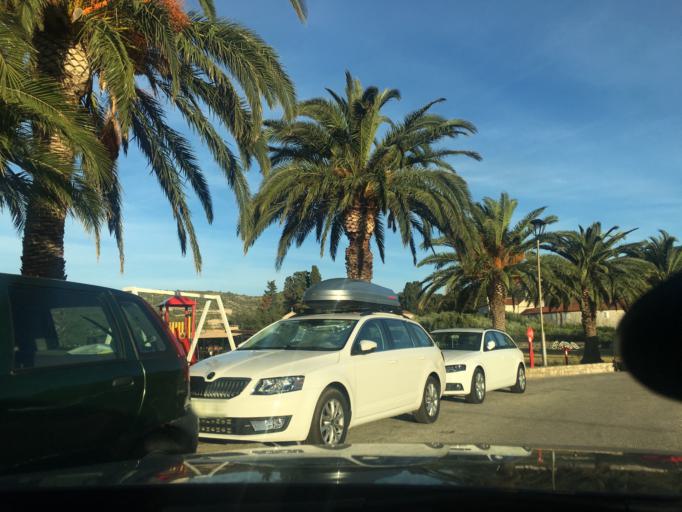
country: HR
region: Splitsko-Dalmatinska
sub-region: Grad Vis
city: Vis
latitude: 43.0636
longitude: 16.1877
